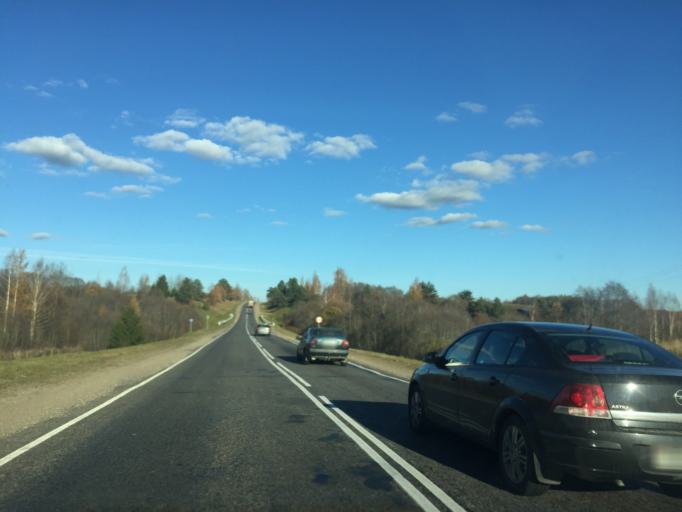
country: BY
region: Vitebsk
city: Dzisna
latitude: 55.2621
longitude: 28.1268
